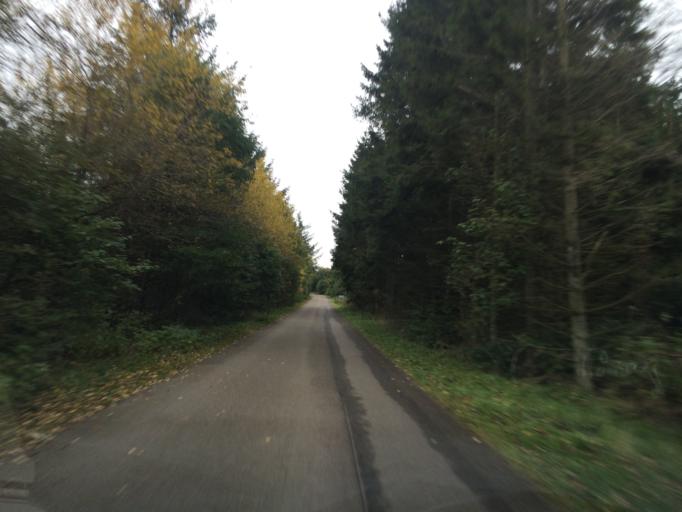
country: DK
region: Central Jutland
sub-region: Holstebro Kommune
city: Ulfborg
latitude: 56.2370
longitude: 8.4212
